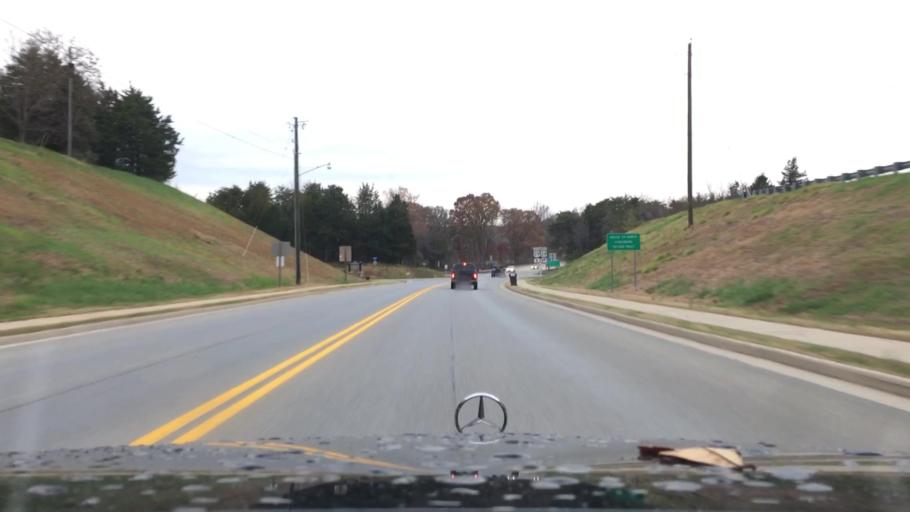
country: US
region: Virginia
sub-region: Campbell County
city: Altavista
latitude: 37.1257
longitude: -79.3060
